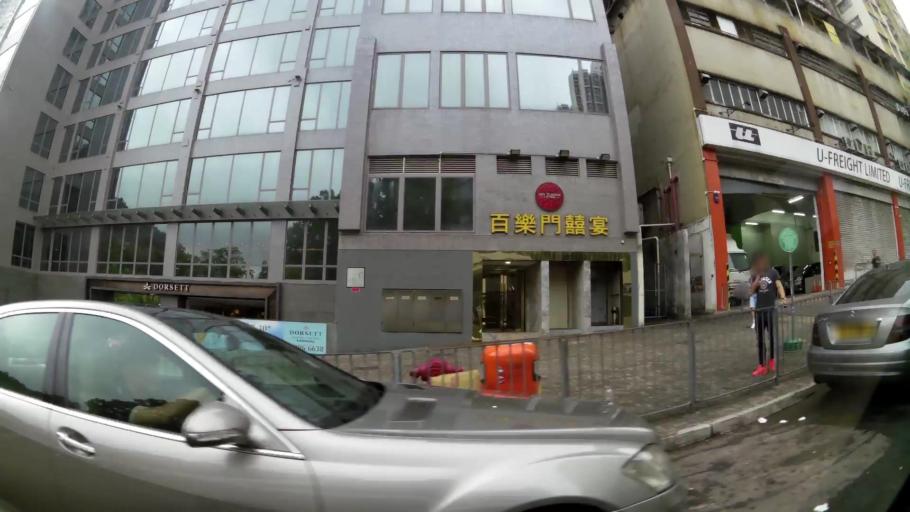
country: HK
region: Tsuen Wan
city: Tsuen Wan
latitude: 22.3704
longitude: 114.1294
